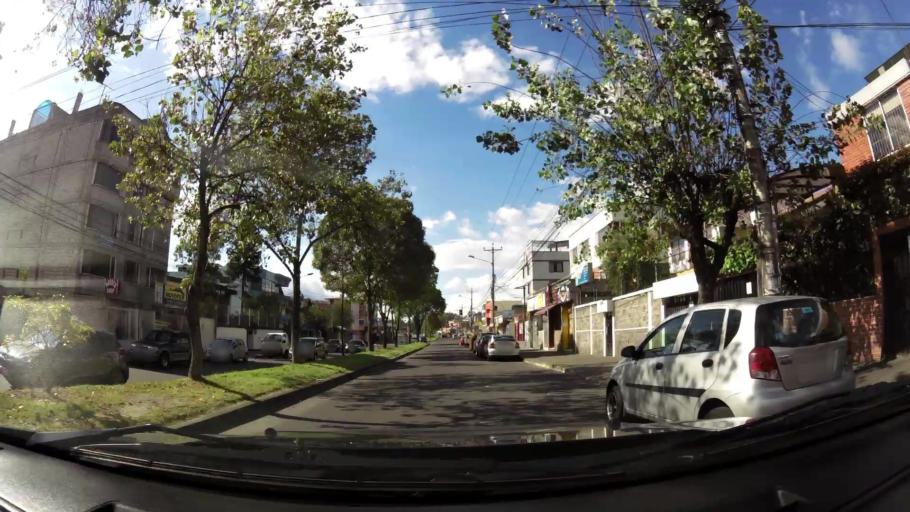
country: EC
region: Pichincha
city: Quito
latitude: -0.1206
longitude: -78.4844
